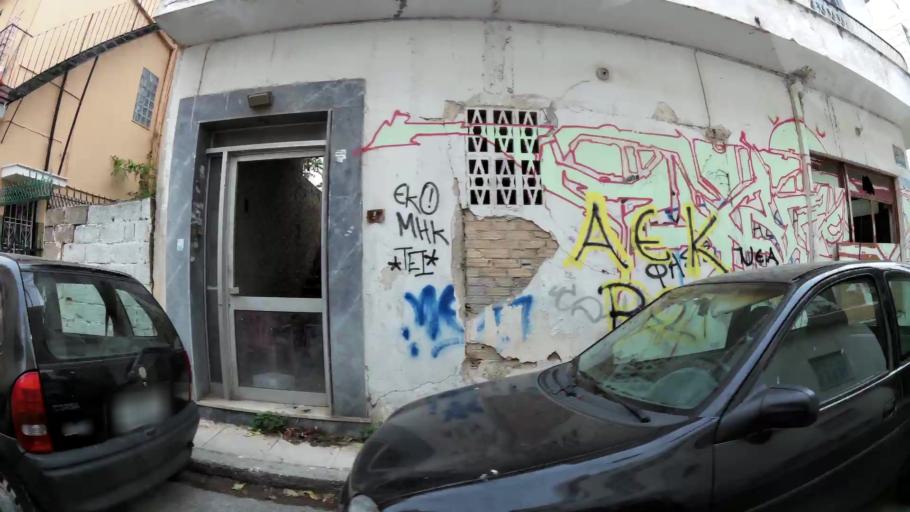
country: GR
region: Attica
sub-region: Nomarchia Athinas
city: Nea Ionia
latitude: 38.0460
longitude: 23.7556
